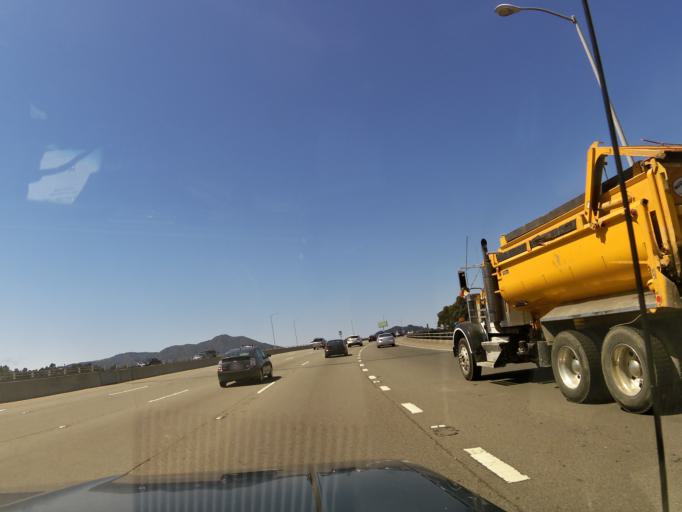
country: US
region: California
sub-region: Marin County
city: Marin City
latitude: 37.8793
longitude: -122.5156
